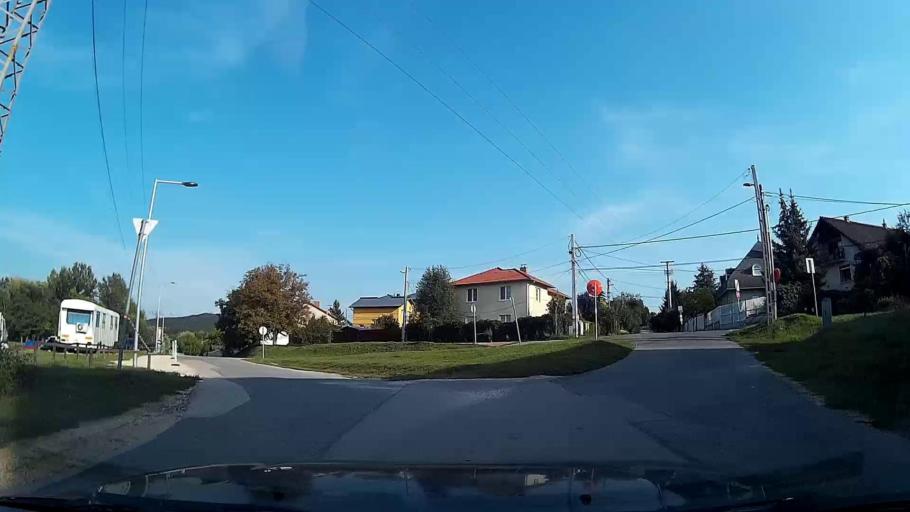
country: HU
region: Pest
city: Budaors
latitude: 47.4399
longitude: 18.9689
